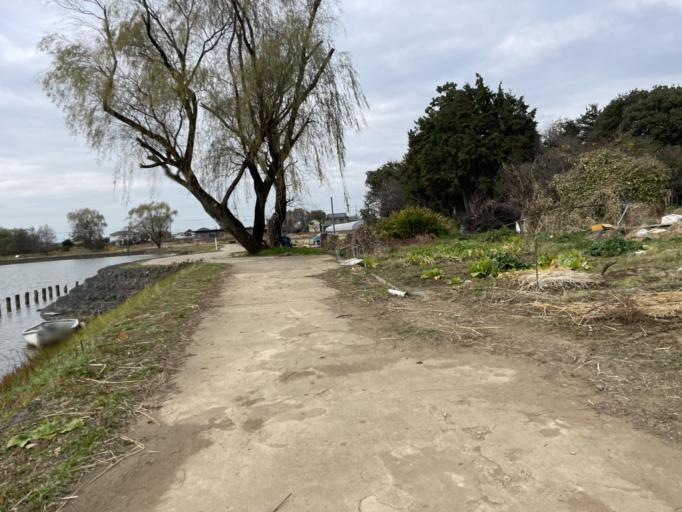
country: JP
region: Saitama
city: Shiraoka
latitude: 36.0220
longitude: 139.6452
